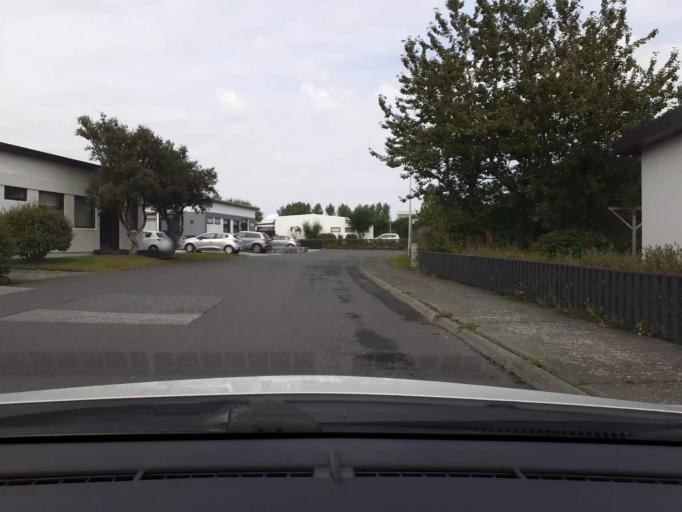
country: IS
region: Southern Peninsula
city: Reykjanesbaer
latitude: 63.9879
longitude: -22.5575
